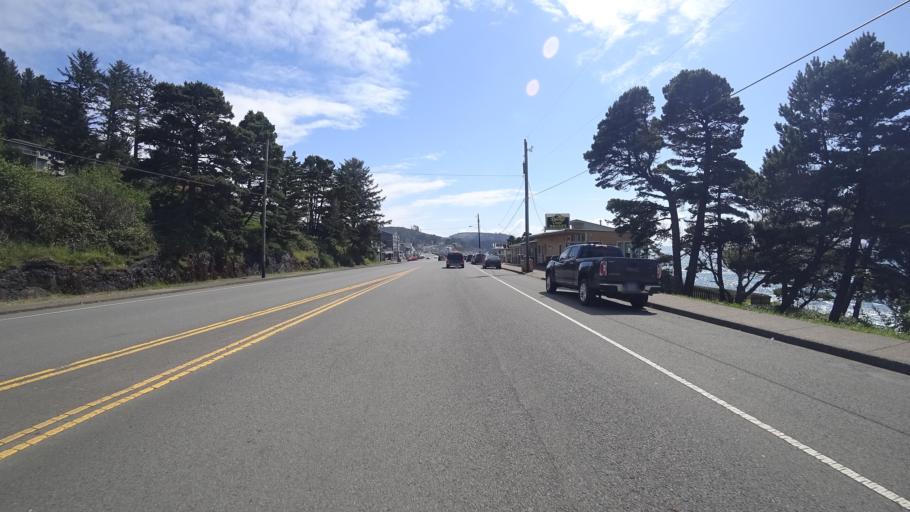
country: US
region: Oregon
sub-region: Lincoln County
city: Depoe Bay
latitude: 44.8144
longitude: -124.0625
